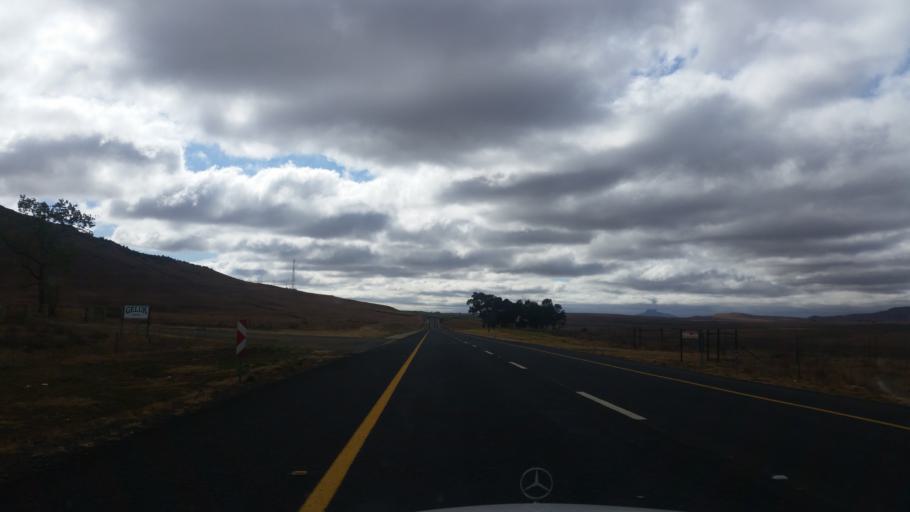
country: ZA
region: Orange Free State
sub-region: Thabo Mofutsanyana District Municipality
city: Phuthaditjhaba
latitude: -28.3125
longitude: 28.7520
